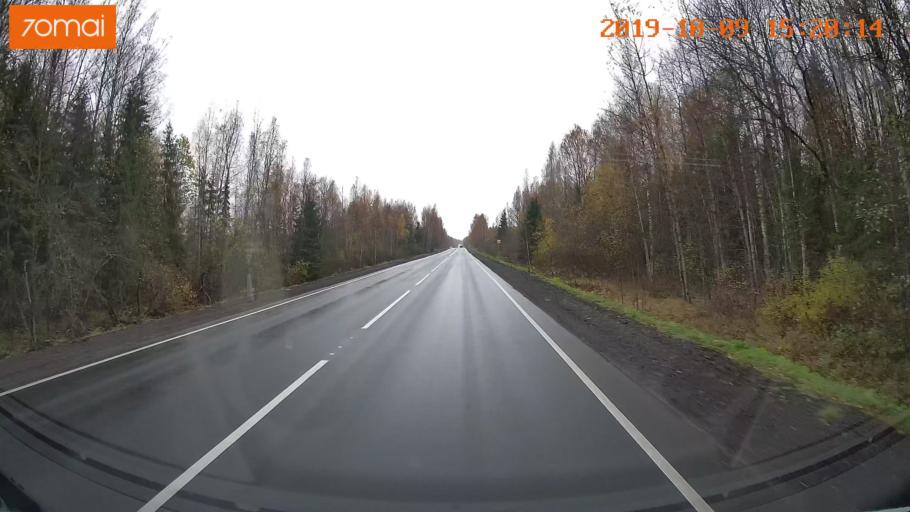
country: RU
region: Kostroma
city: Susanino
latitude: 58.0666
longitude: 41.5416
